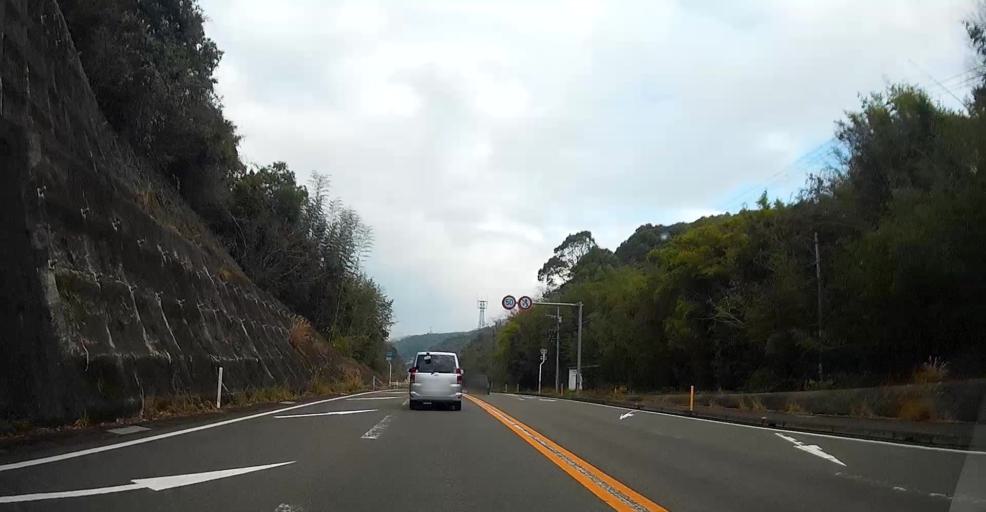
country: JP
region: Kumamoto
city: Yatsushiro
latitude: 32.5589
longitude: 130.4150
